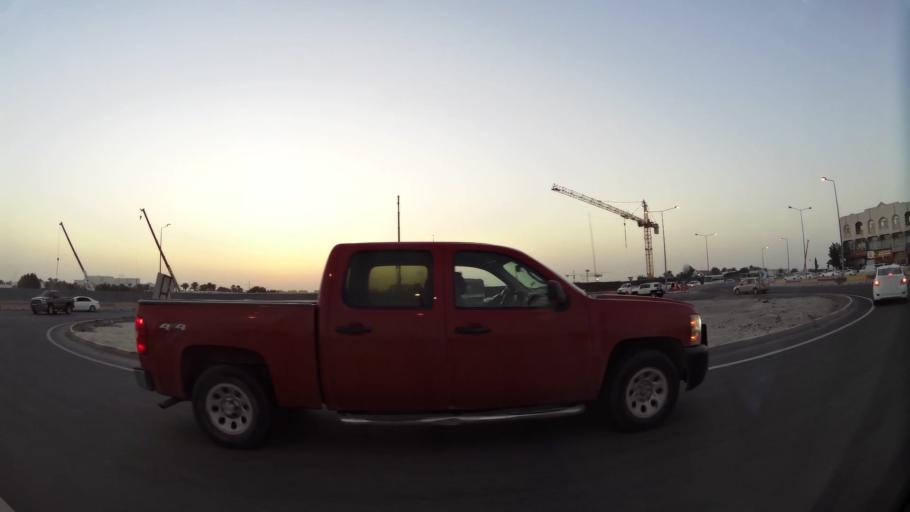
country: QA
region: Baladiyat ar Rayyan
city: Ar Rayyan
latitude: 25.2986
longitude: 51.4655
